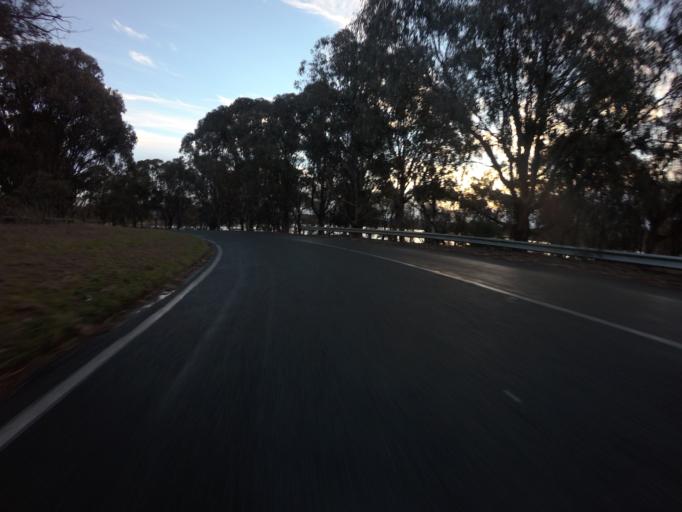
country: AU
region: Australian Capital Territory
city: Acton
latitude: -35.2970
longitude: 149.1076
